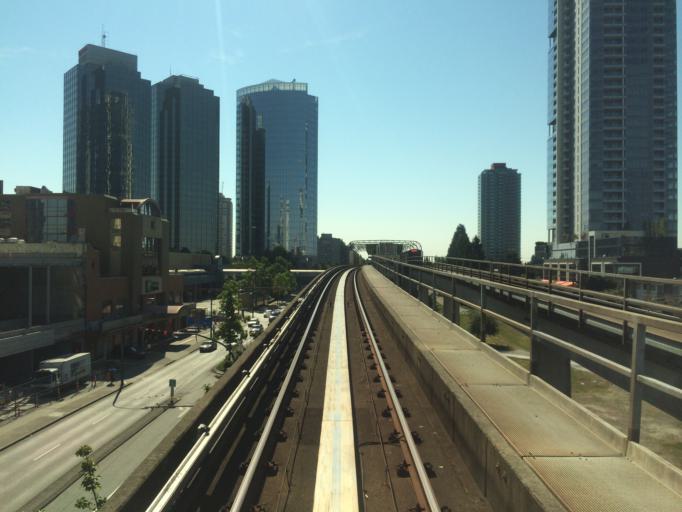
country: CA
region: British Columbia
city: Burnaby
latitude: 49.2266
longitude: -123.0054
